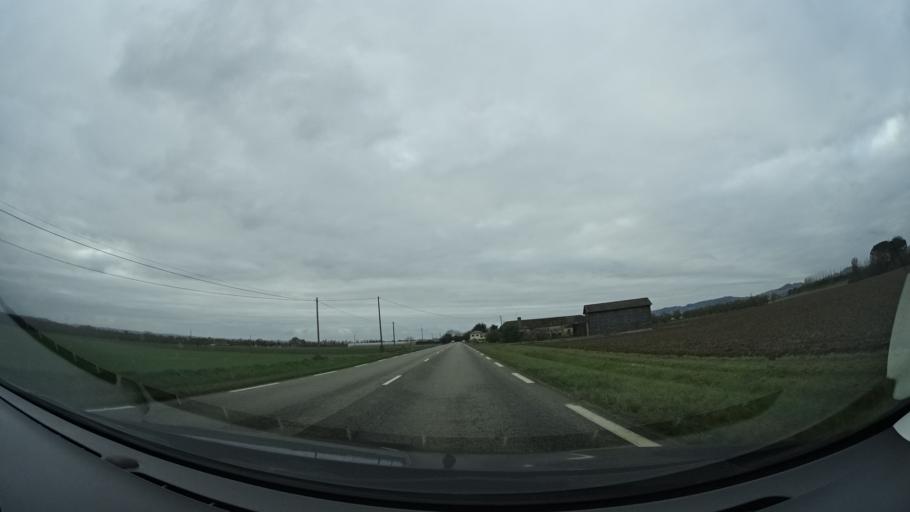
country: FR
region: Aquitaine
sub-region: Departement du Lot-et-Garonne
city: Clairac
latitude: 44.3496
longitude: 0.4209
